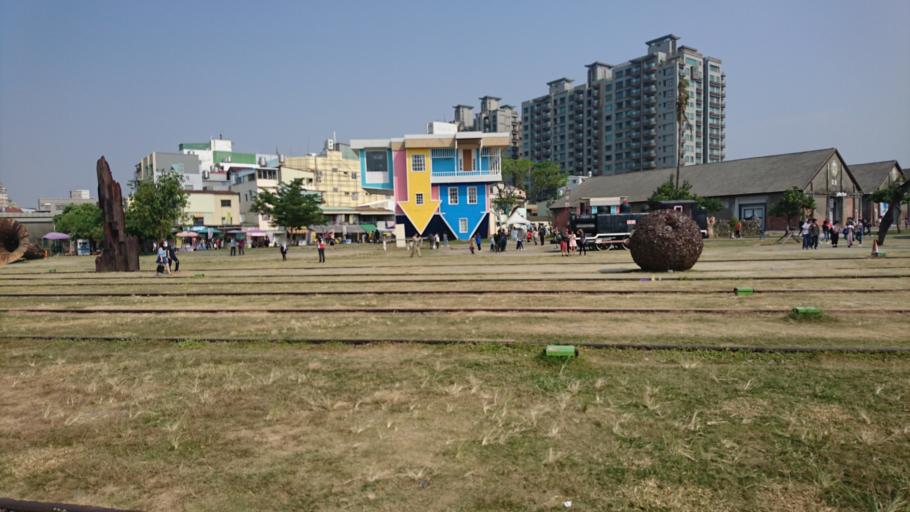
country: TW
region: Kaohsiung
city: Kaohsiung
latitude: 22.6210
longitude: 120.2769
